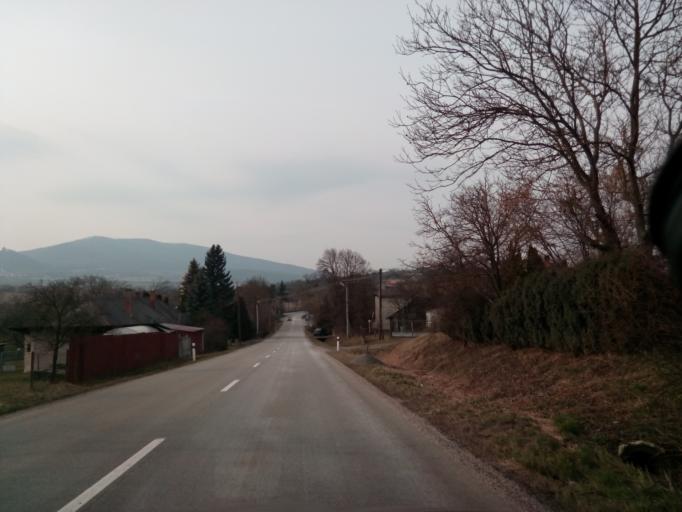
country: SK
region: Kosicky
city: Secovce
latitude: 48.6275
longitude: 21.5272
